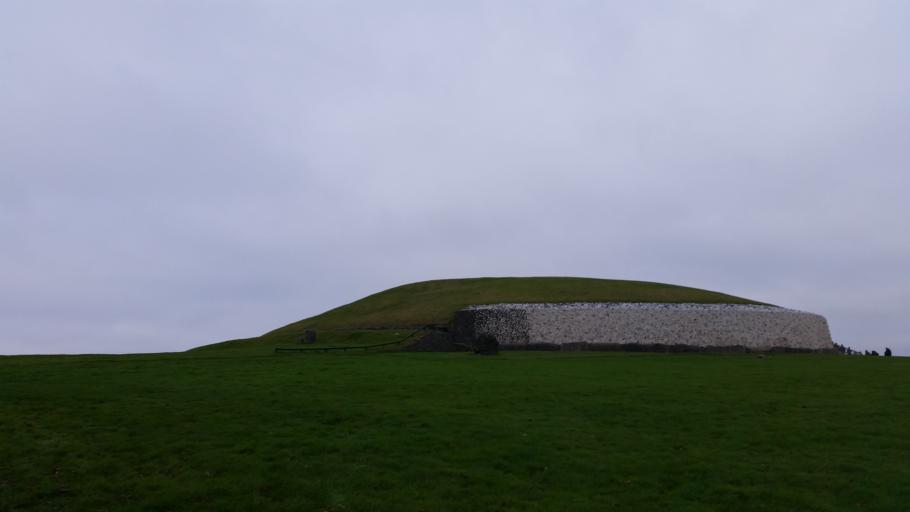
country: IE
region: Leinster
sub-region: Lu
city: Tullyallen
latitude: 53.6939
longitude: -6.4763
